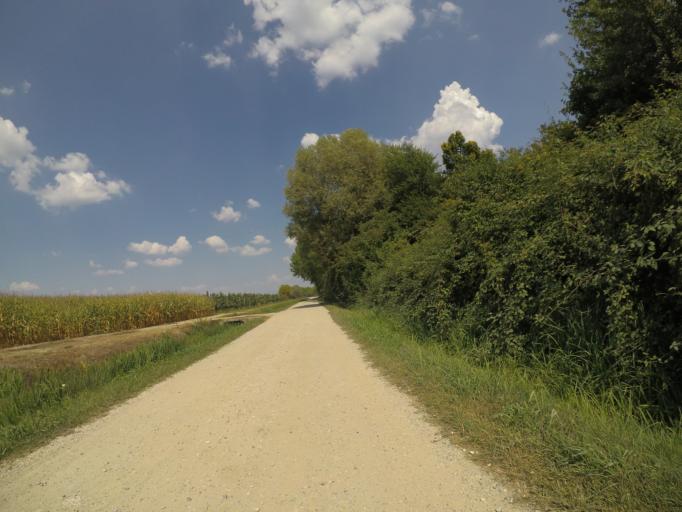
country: IT
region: Friuli Venezia Giulia
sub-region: Provincia di Udine
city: Bertiolo
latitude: 45.9261
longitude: 13.0671
